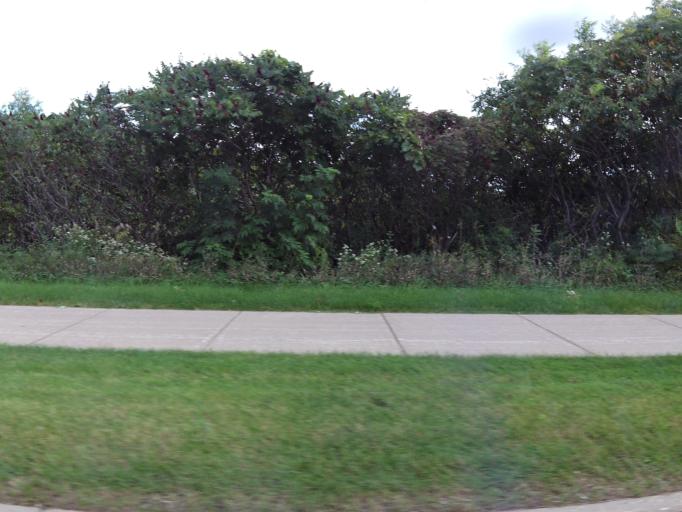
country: US
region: Minnesota
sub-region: Dakota County
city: Inver Grove Heights
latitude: 44.8220
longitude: -93.0417
